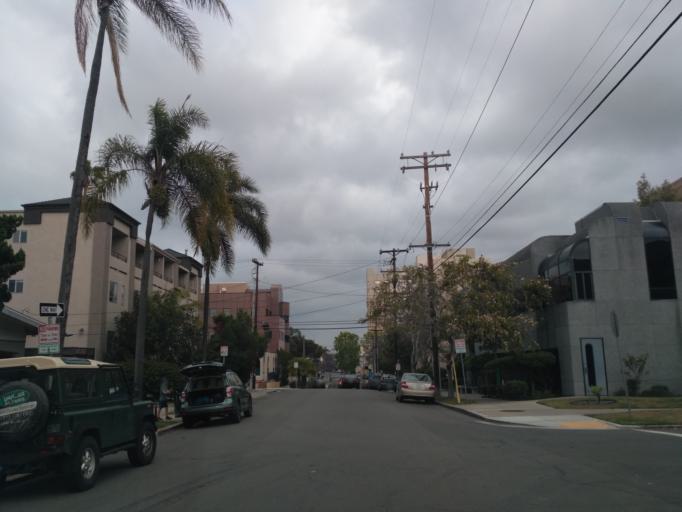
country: US
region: California
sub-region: San Diego County
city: San Diego
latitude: 32.7518
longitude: -117.1630
